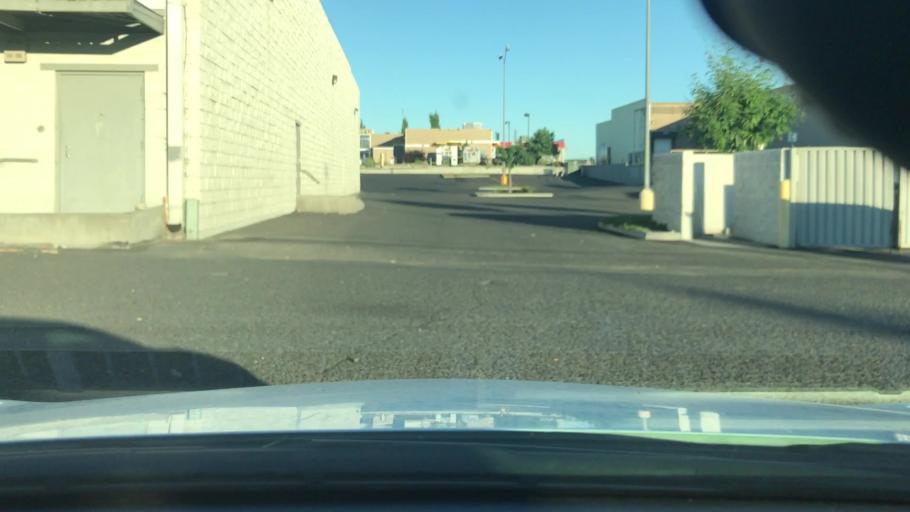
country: US
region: Washington
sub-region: Grant County
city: Moses Lake
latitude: 47.1400
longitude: -119.2760
